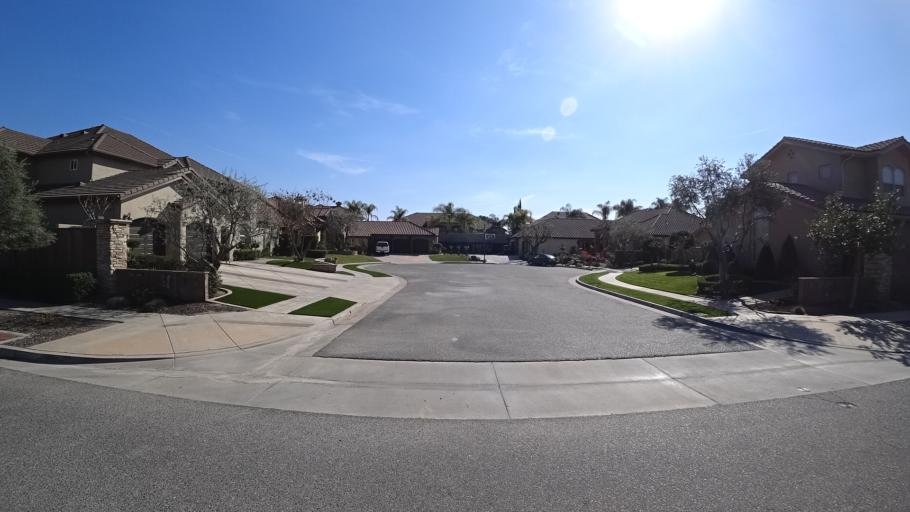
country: US
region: California
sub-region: Fresno County
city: Clovis
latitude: 36.8927
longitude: -119.7466
